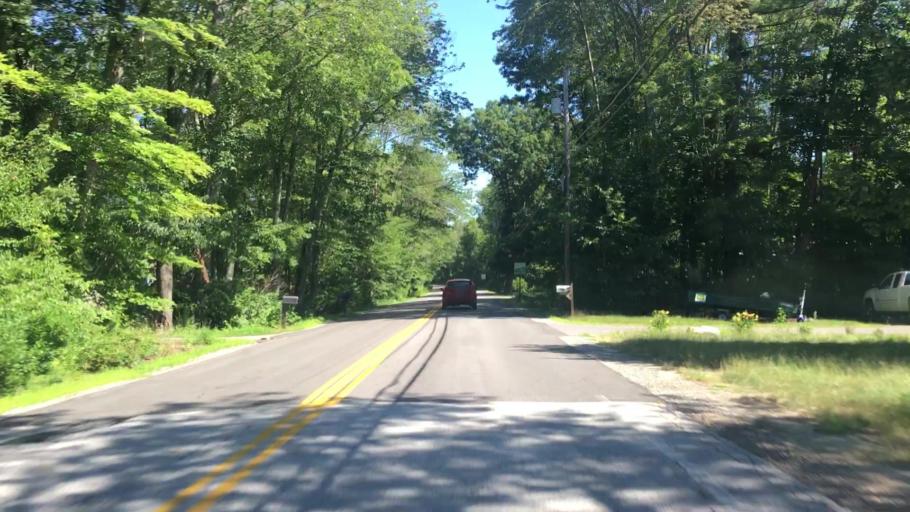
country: US
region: New Hampshire
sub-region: Rockingham County
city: Auburn
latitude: 43.0289
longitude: -71.3825
